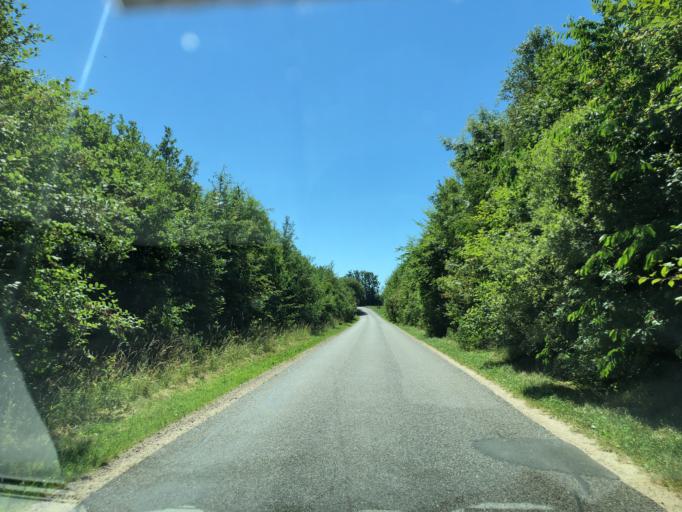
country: DK
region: Central Jutland
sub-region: Viborg Kommune
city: Viborg
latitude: 56.5324
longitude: 9.4792
